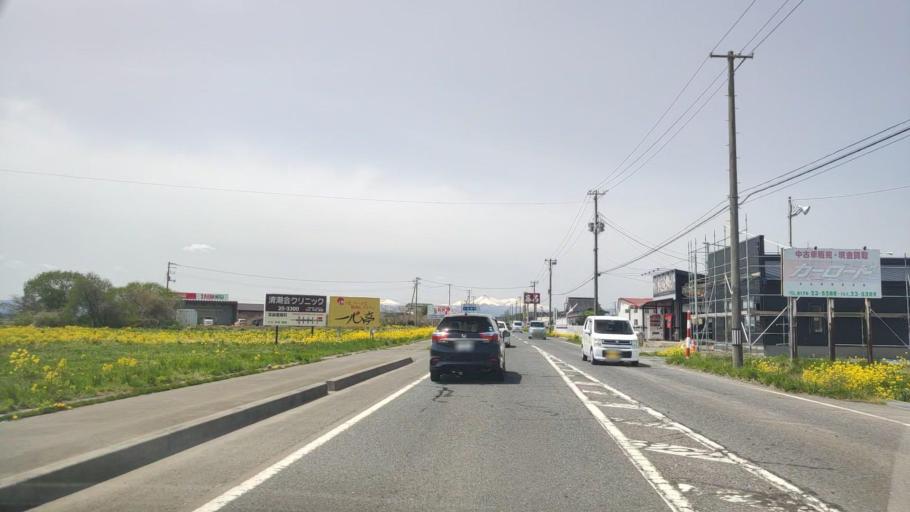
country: JP
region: Aomori
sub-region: Misawa Shi
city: Inuotose
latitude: 40.6109
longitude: 141.2723
